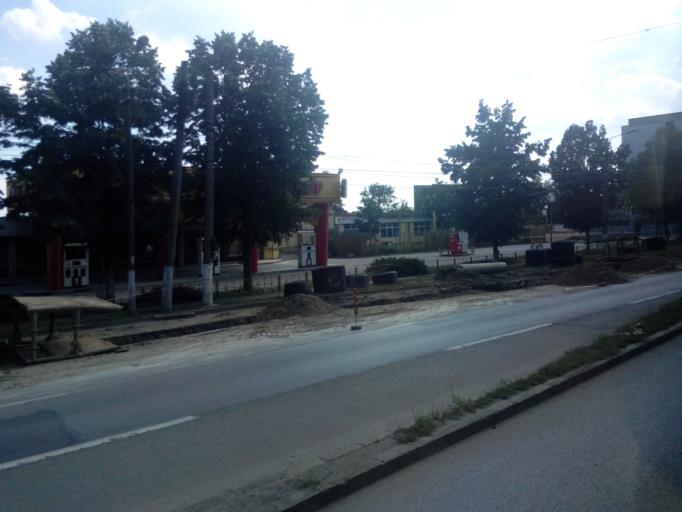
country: RO
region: Timis
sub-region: Comuna Ghiroda
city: Ghiroda
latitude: 45.7697
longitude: 21.2688
